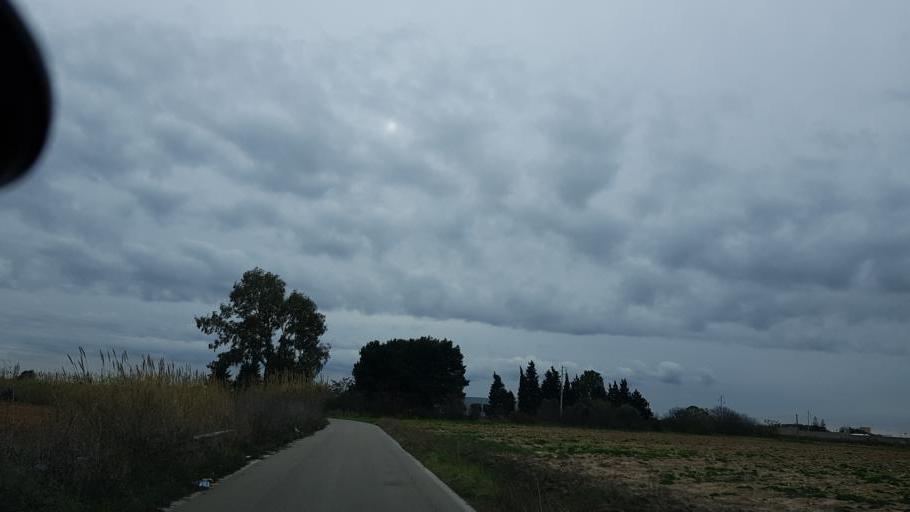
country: IT
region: Apulia
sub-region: Provincia di Brindisi
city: La Rosa
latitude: 40.6125
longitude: 17.9504
